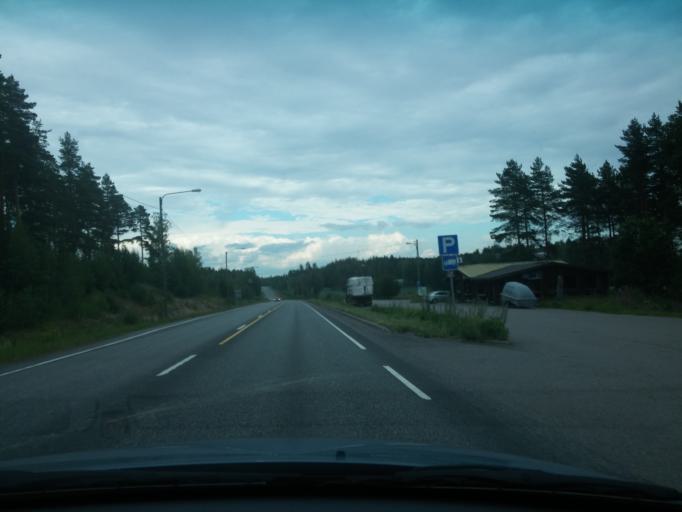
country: FI
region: Haeme
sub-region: Riihimaeki
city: Loppi
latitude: 60.7271
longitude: 24.5181
